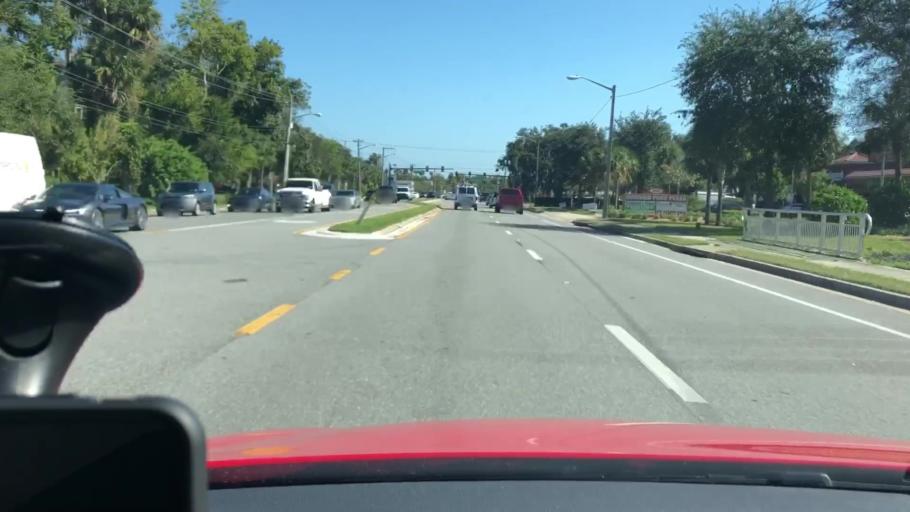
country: US
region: Florida
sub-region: Volusia County
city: Ormond Beach
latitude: 29.2799
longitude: -81.0706
